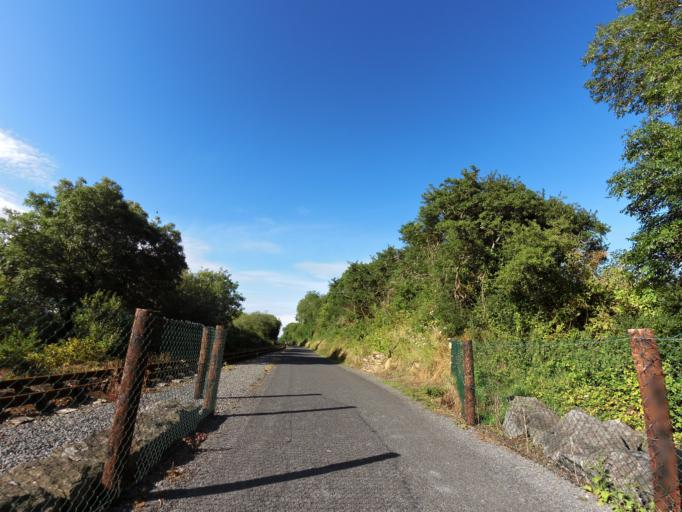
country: IE
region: Leinster
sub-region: Kilkenny
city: Mooncoin
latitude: 52.2495
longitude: -7.1959
